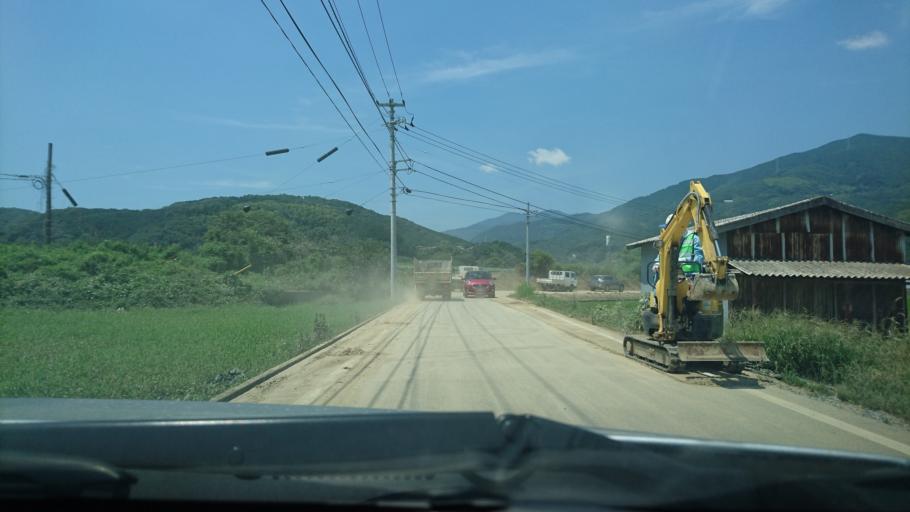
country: JP
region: Ehime
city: Ozu
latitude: 33.5346
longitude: 132.5671
